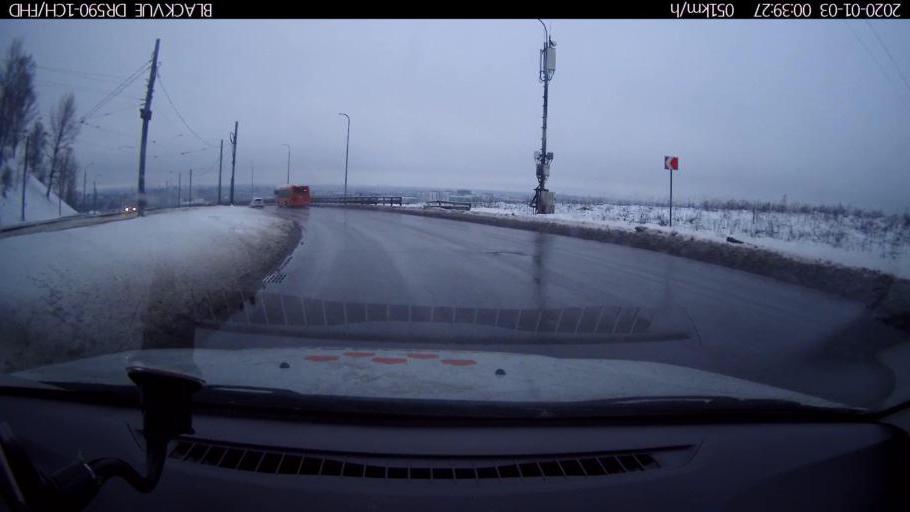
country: RU
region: Nizjnij Novgorod
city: Nizhniy Novgorod
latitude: 56.3044
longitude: 43.9723
